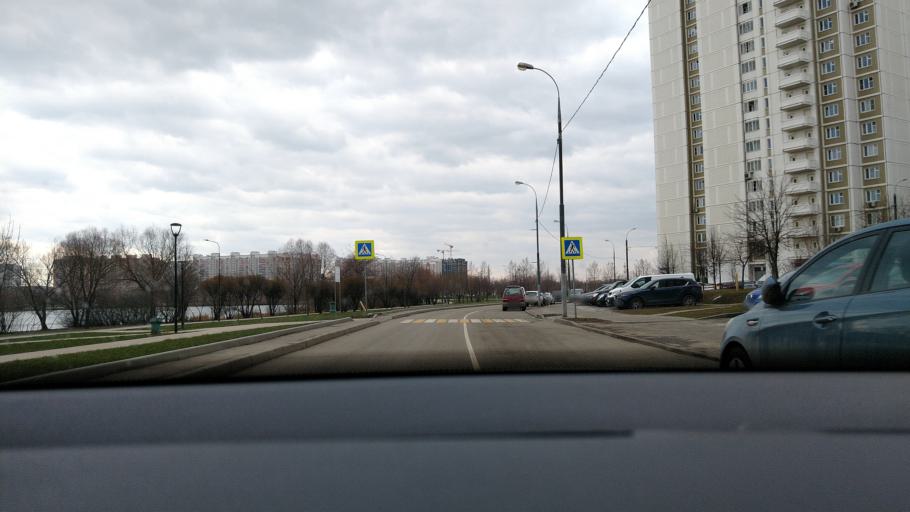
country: RU
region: Moskovskaya
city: Kommunarka
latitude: 55.5328
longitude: 37.5041
